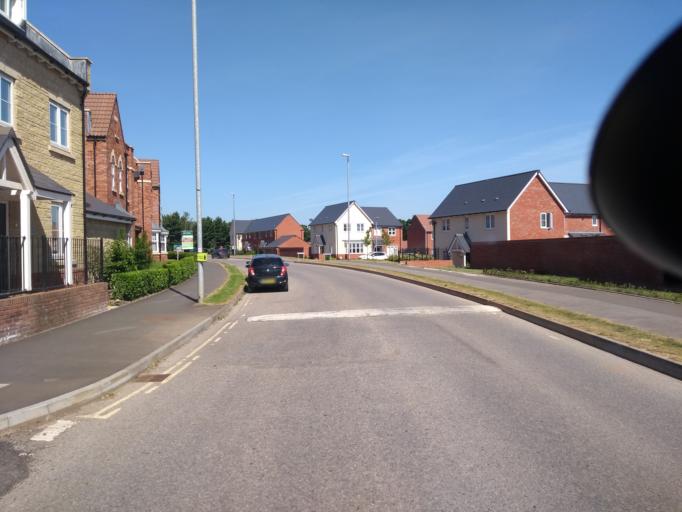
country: GB
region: England
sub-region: Somerset
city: North Petherton
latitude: 51.1093
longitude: -3.0098
